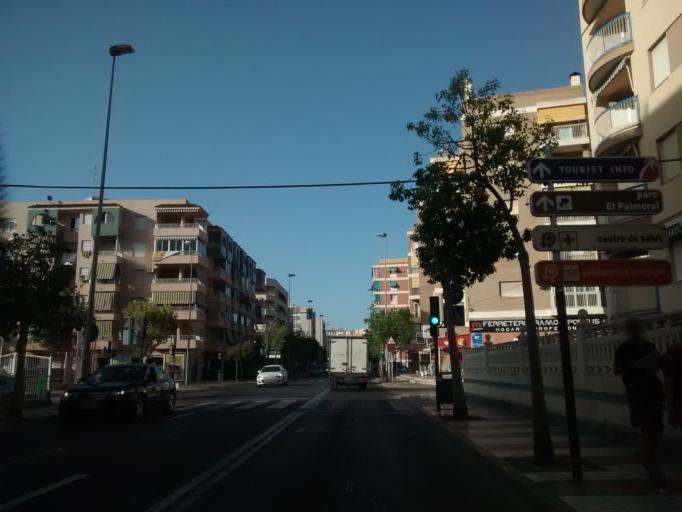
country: ES
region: Valencia
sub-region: Provincia de Alicante
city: Santa Pola
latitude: 38.1932
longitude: -0.5615
